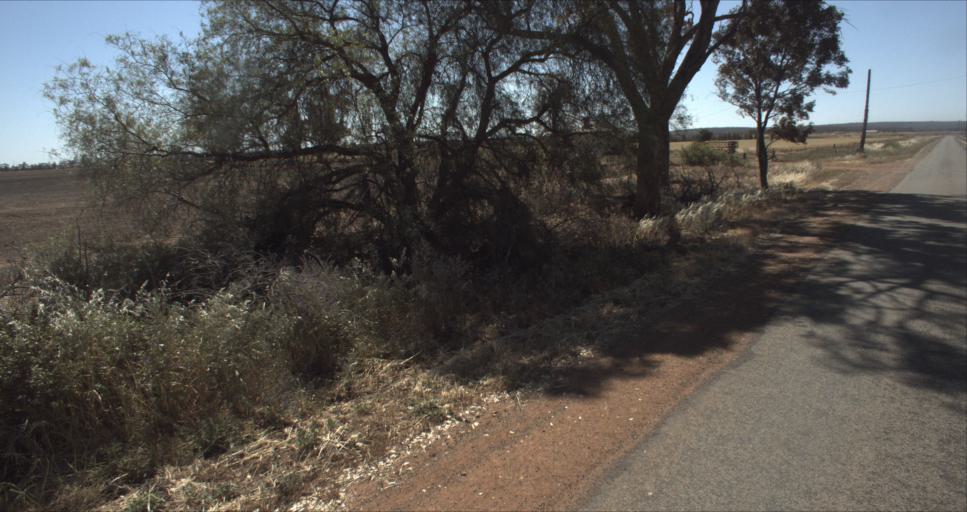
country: AU
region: New South Wales
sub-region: Leeton
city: Leeton
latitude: -34.4741
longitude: 146.4164
